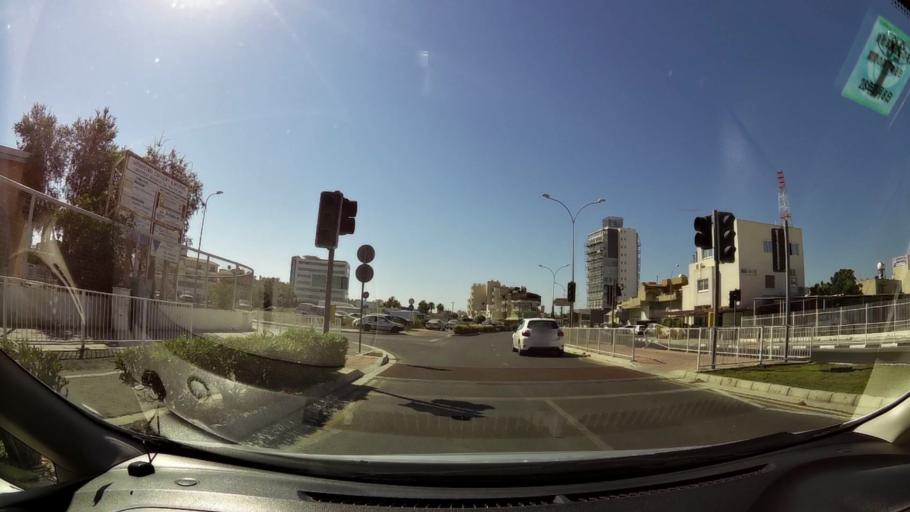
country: CY
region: Larnaka
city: Larnaca
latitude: 34.9326
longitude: 33.6282
